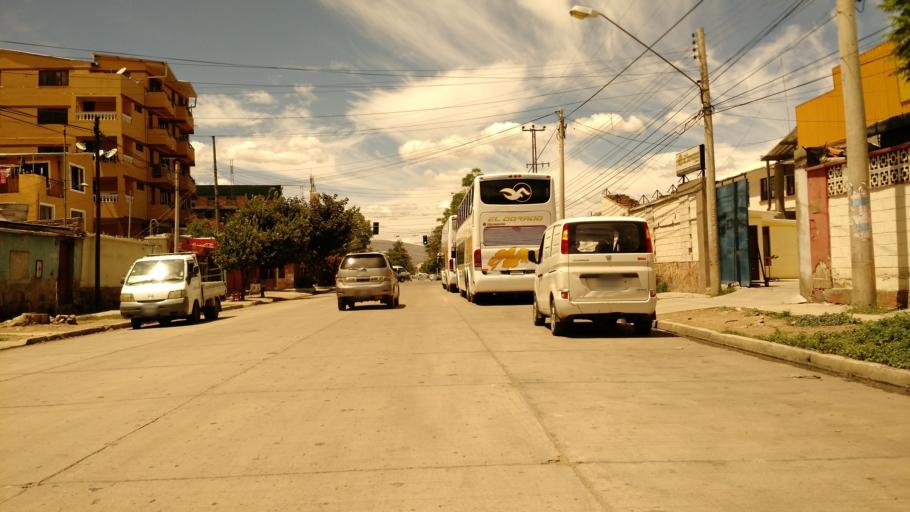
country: BO
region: Cochabamba
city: Cochabamba
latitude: -17.3987
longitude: -66.1665
